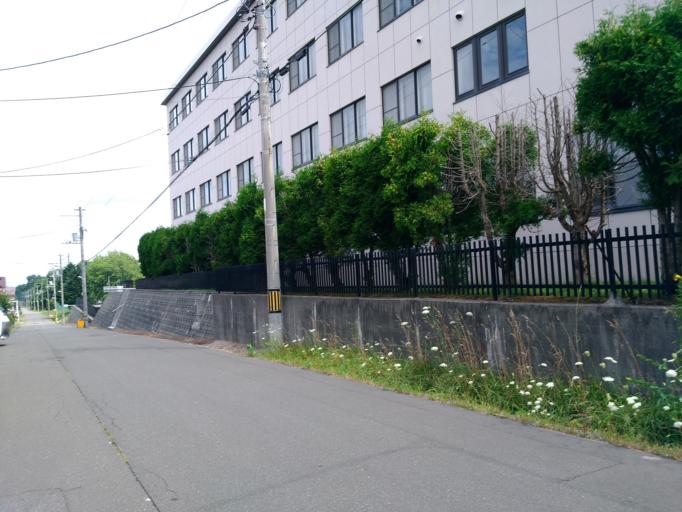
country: JP
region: Hokkaido
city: Ebetsu
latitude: 43.0670
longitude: 141.4996
